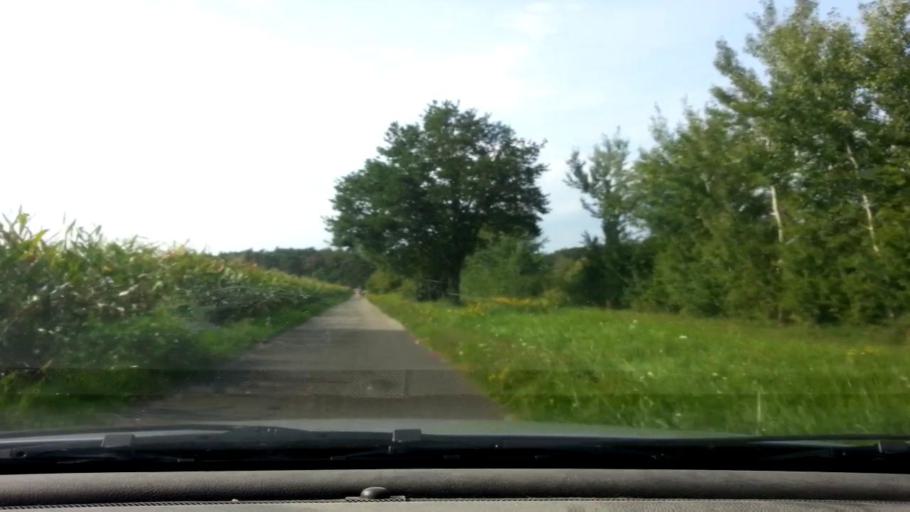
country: DE
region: Bavaria
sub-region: Upper Franconia
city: Pettstadt
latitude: 49.8474
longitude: 10.9444
